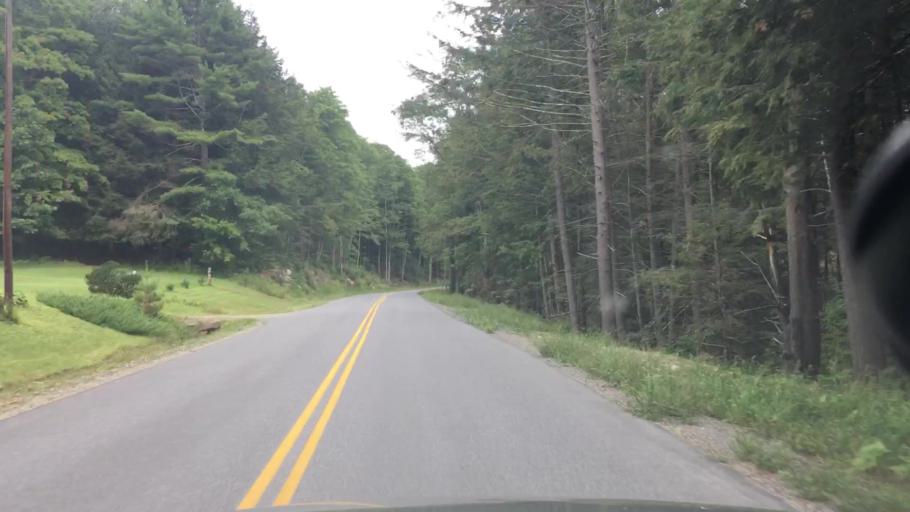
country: US
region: Massachusetts
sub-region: Franklin County
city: Colrain
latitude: 42.7699
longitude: -72.7657
